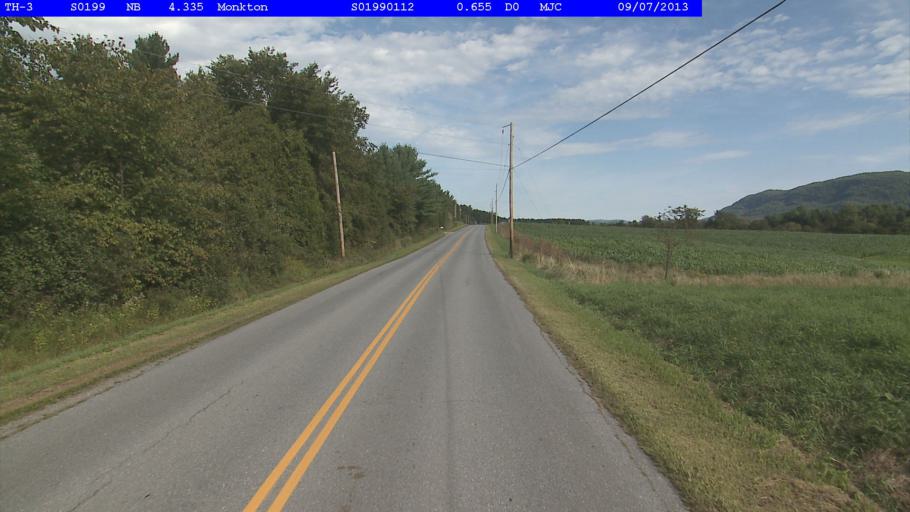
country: US
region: Vermont
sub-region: Addison County
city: Bristol
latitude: 44.1900
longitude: -73.1083
